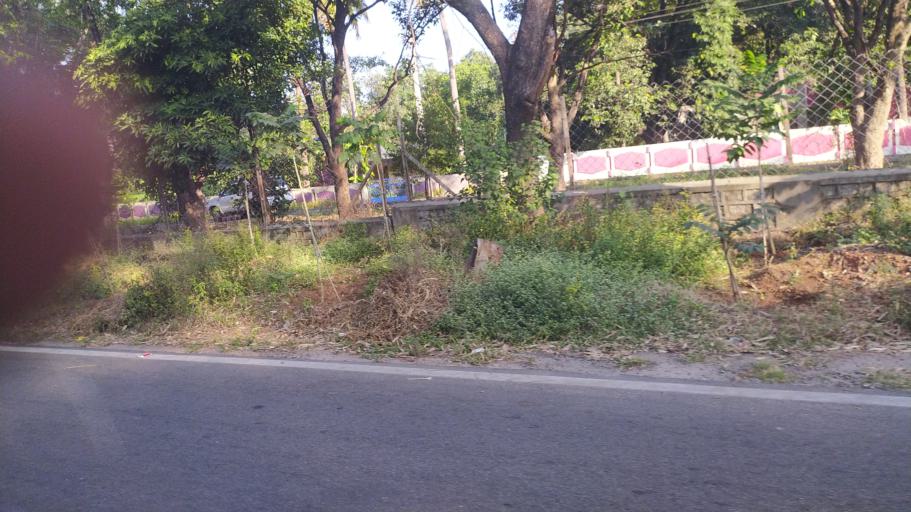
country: IN
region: Telangana
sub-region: Hyderabad
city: Hyderabad
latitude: 17.3295
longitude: 78.4138
